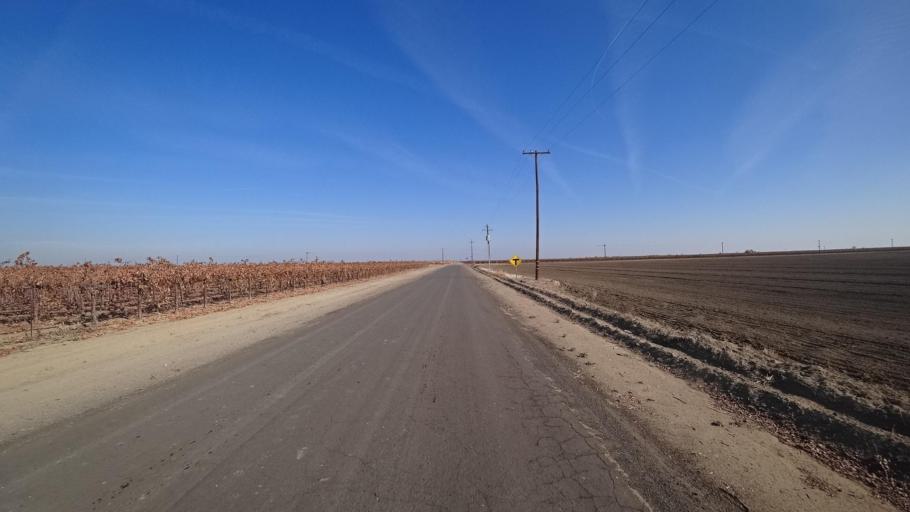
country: US
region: California
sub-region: Kern County
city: Wasco
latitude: 35.6887
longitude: -119.3861
